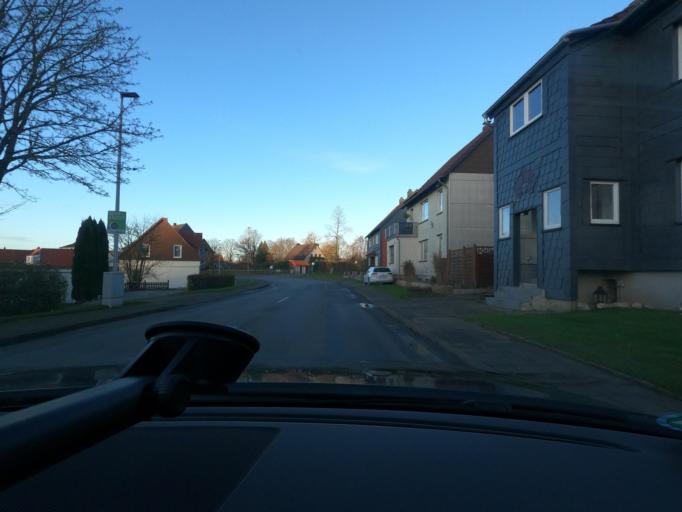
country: DE
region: Lower Saxony
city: Badenhausen
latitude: 51.7649
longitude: 10.2117
